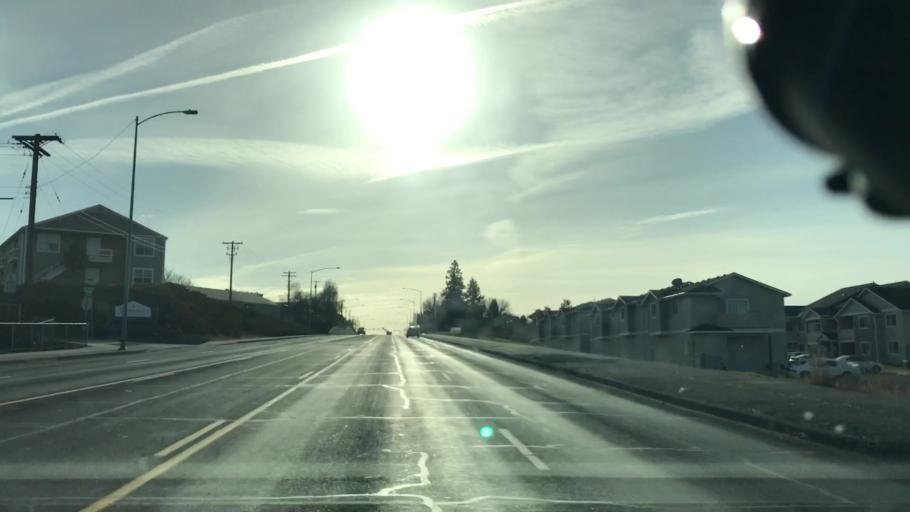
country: US
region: Washington
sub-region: Grant County
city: Moses Lake
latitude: 47.1259
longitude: -119.2689
